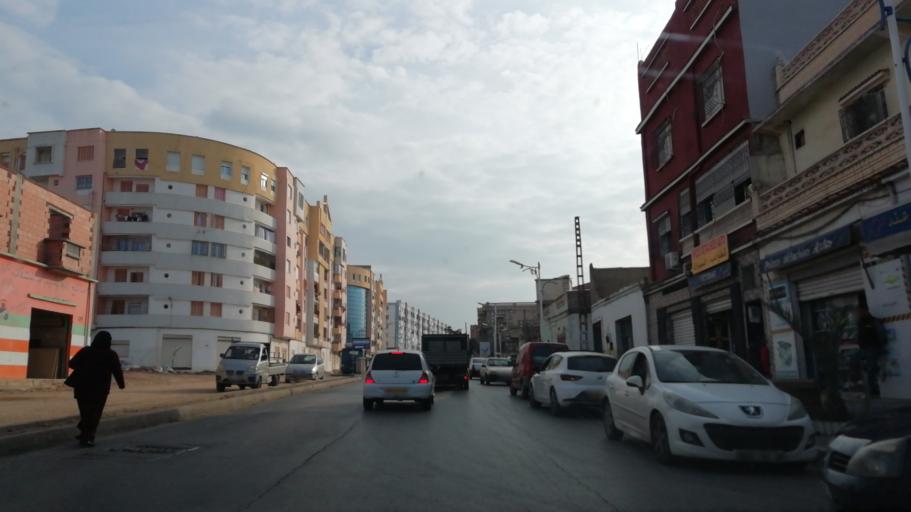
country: DZ
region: Mostaganem
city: Mostaganem
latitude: 35.8947
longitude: 0.0759
